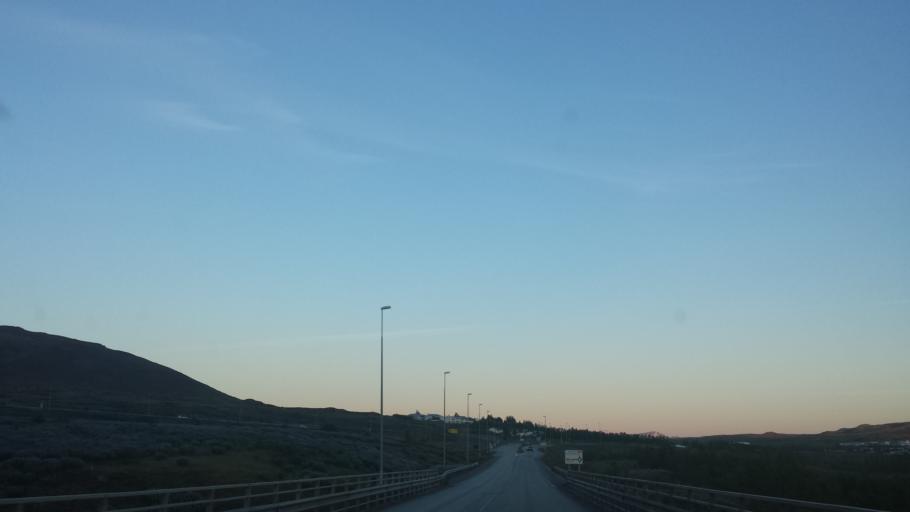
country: IS
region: Capital Region
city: Mosfellsbaer
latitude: 64.1806
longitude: -21.6787
